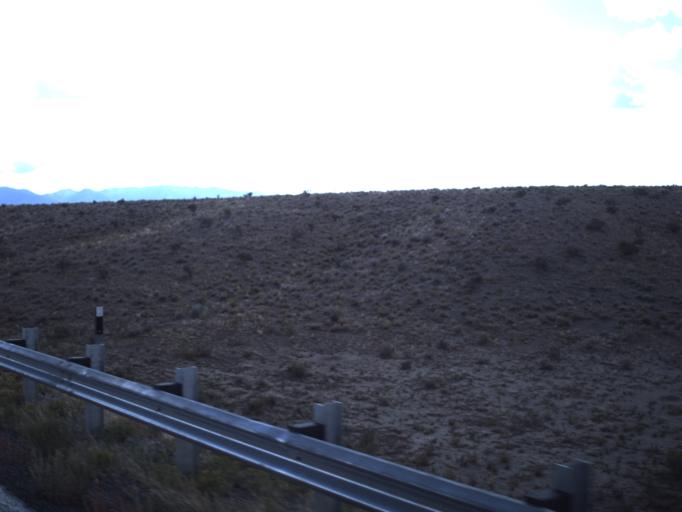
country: US
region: Utah
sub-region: Beaver County
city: Milford
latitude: 38.5675
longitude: -113.7773
